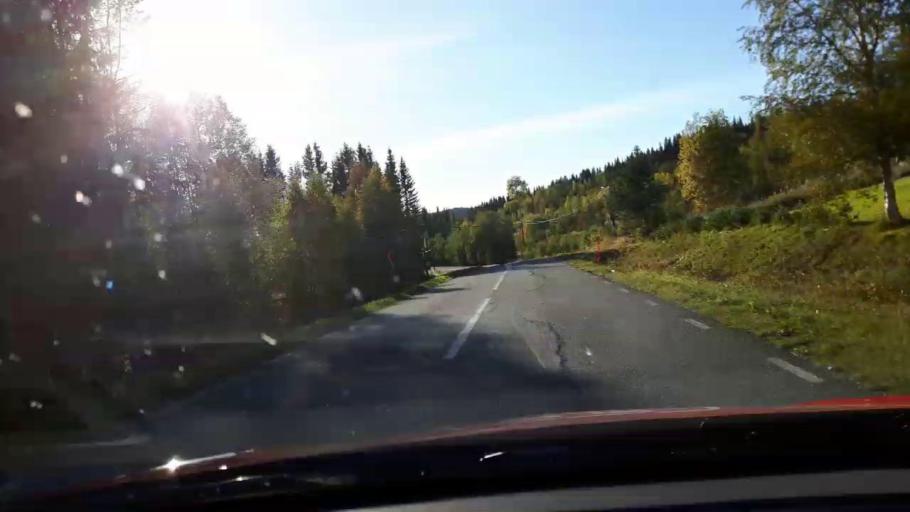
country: SE
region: Jaemtland
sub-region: OEstersunds Kommun
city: Lit
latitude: 63.8220
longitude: 14.8424
